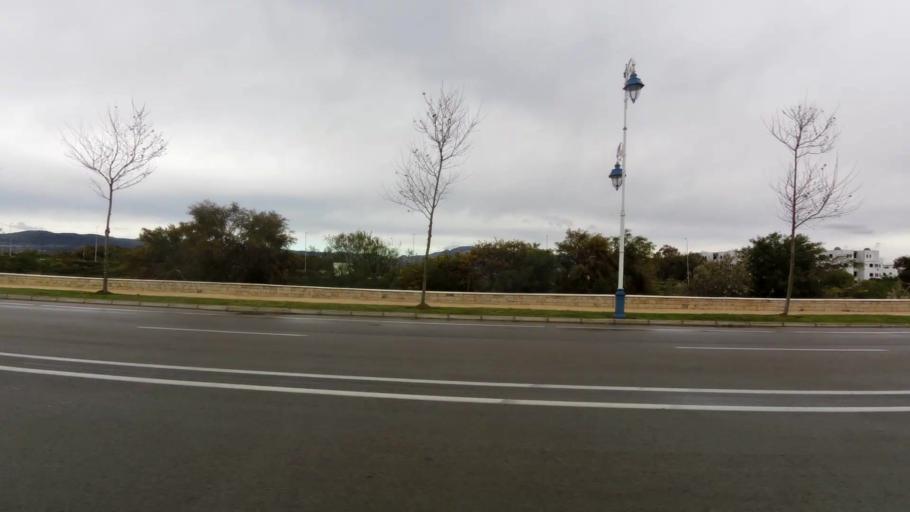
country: MA
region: Tanger-Tetouan
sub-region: Tetouan
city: Martil
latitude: 35.6514
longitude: -5.2921
